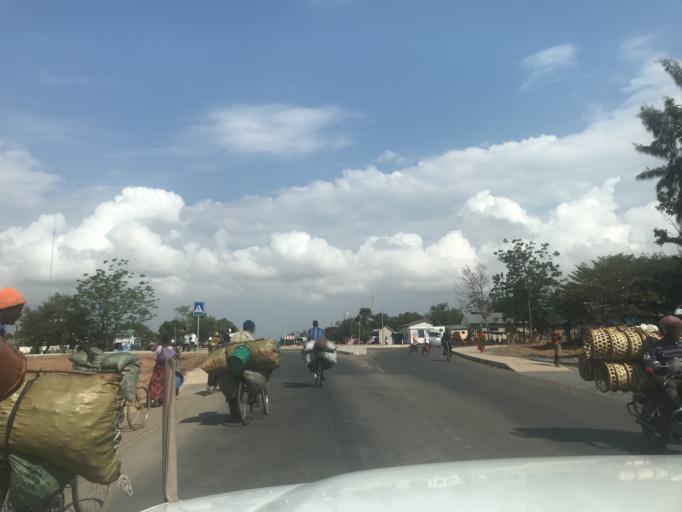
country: TZ
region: Mwanza
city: Usagara
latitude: -2.5554
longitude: 33.0505
